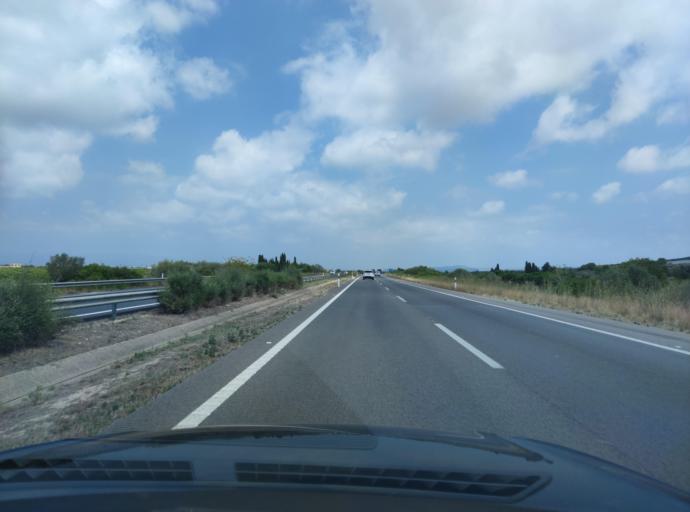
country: ES
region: Valencia
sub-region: Provincia de Castello
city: Vinaros
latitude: 40.5055
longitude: 0.4158
